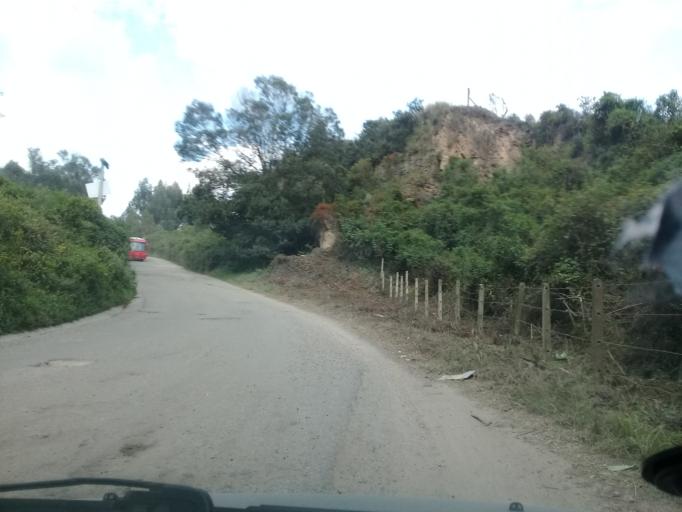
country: CO
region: Cundinamarca
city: El Rosal
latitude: 4.7949
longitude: -74.2171
